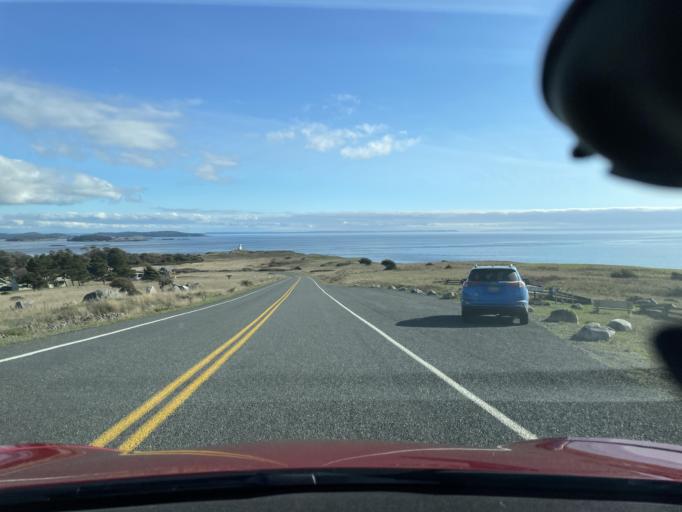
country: US
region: Washington
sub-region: San Juan County
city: Friday Harbor
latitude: 48.4545
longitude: -122.9713
